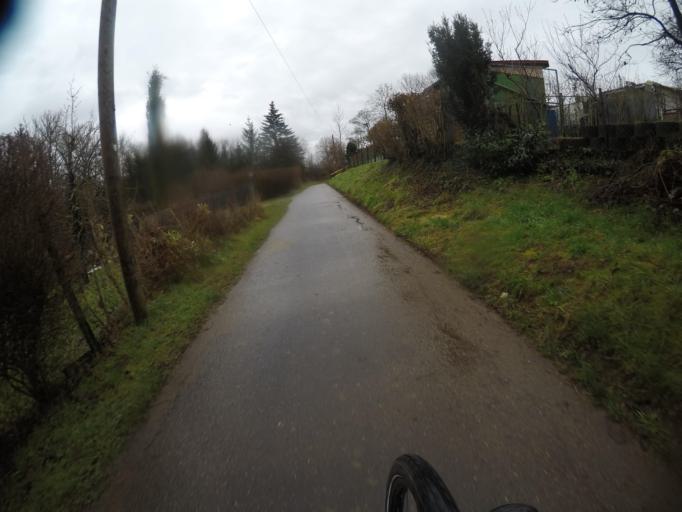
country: DE
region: Baden-Wuerttemberg
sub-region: Regierungsbezirk Stuttgart
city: Bietigheim-Bissingen
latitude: 48.9582
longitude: 9.1166
